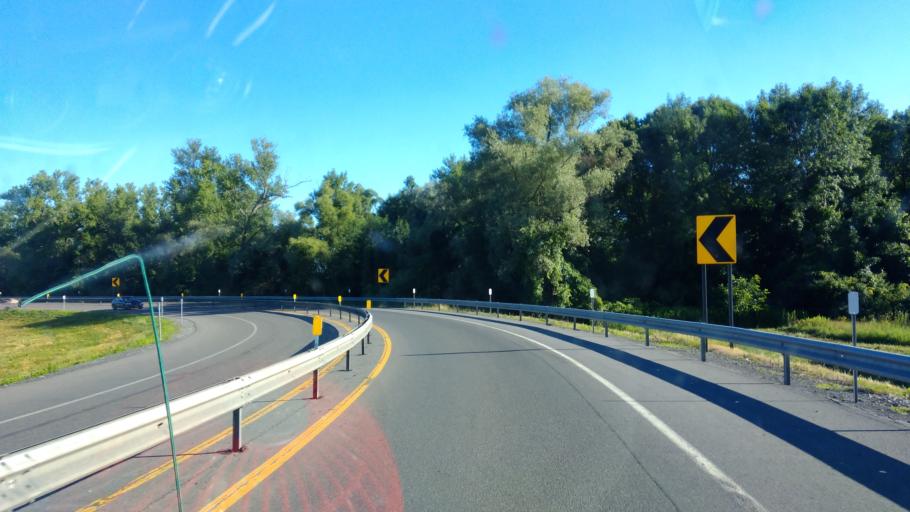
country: US
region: New York
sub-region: Ontario County
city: Phelps
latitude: 42.9561
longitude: -76.9815
